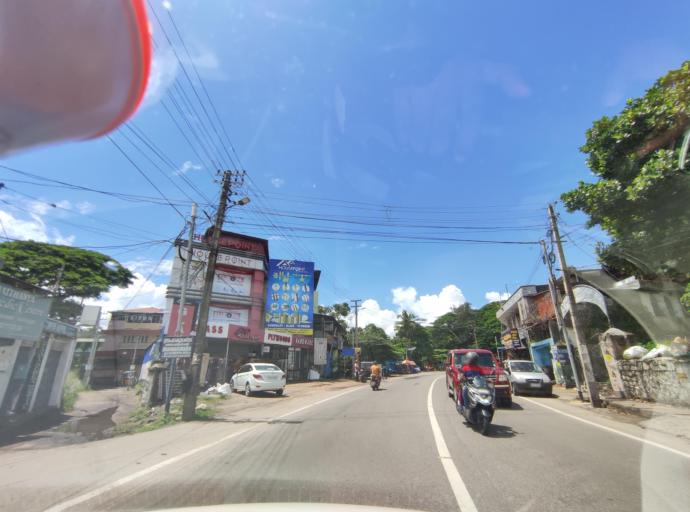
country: IN
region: Kerala
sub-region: Thiruvananthapuram
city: Thiruvananthapuram
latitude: 8.4842
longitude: 76.9567
